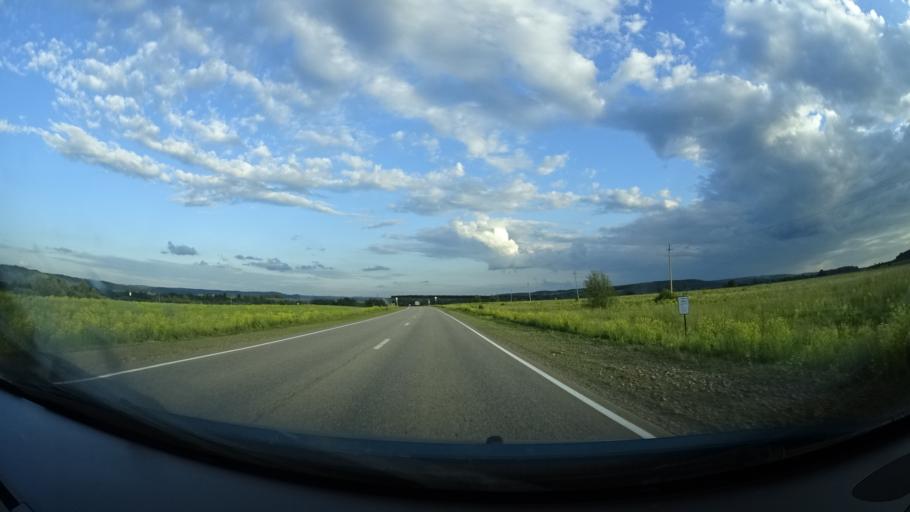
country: RU
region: Perm
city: Barda
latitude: 57.0353
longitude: 55.5481
